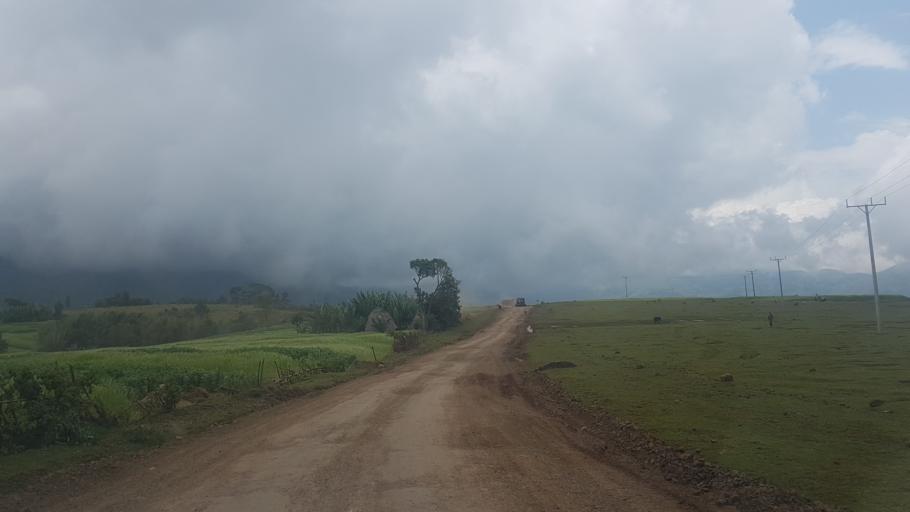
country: ET
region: Southern Nations, Nationalities, and People's Region
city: Arba Minch'
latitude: 6.3245
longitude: 37.5418
